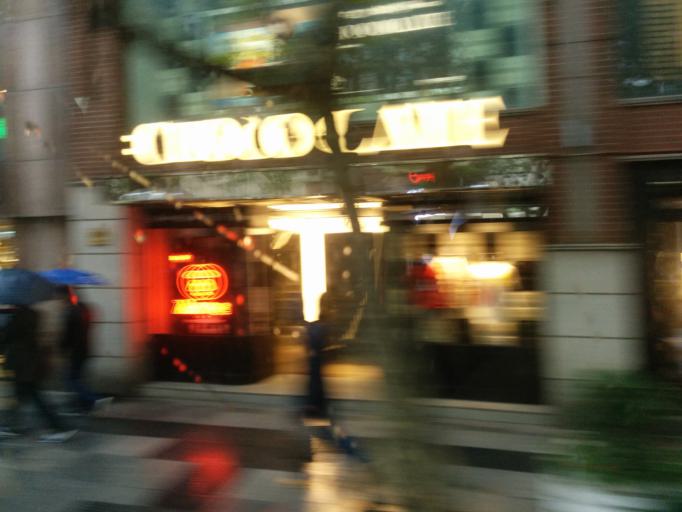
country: CN
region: Shanghai Shi
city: Shanghai
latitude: 31.2306
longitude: 121.4529
